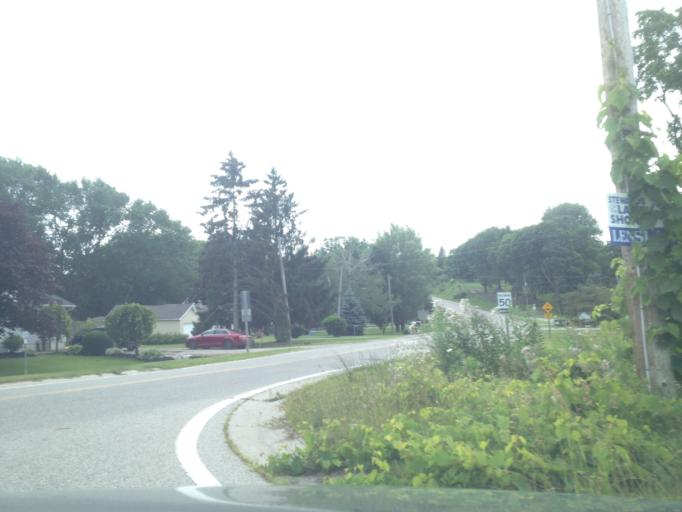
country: CA
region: Ontario
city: Aylmer
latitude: 42.6611
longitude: -81.0154
